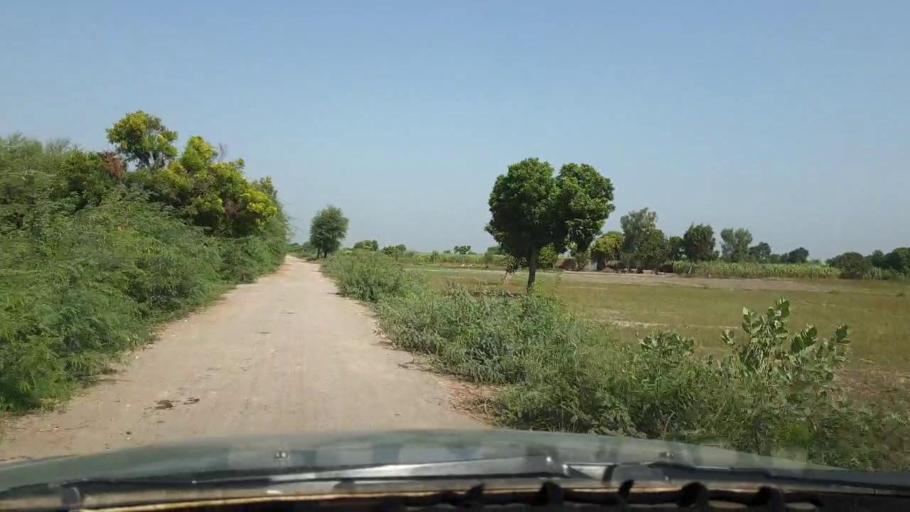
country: PK
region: Sindh
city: Matli
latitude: 25.0910
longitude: 68.6109
